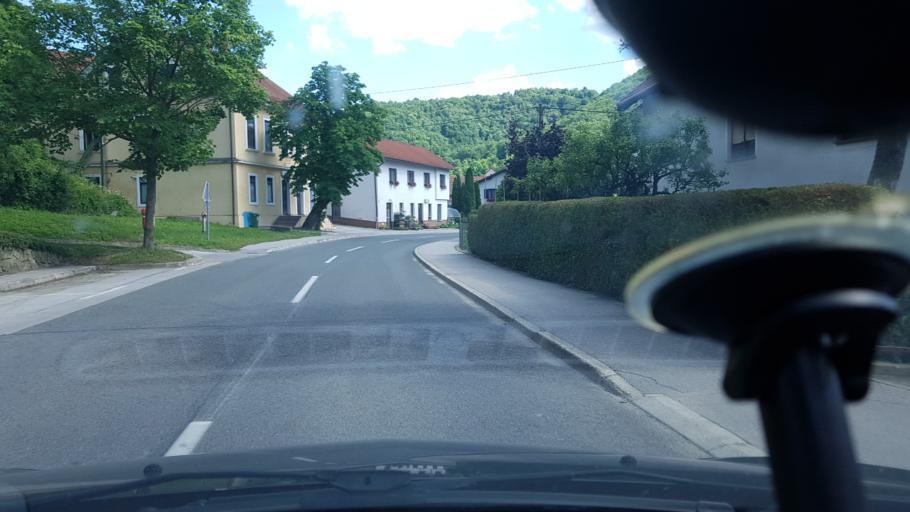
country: SI
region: Rogatec
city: Rogatec
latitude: 46.2268
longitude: 15.6999
